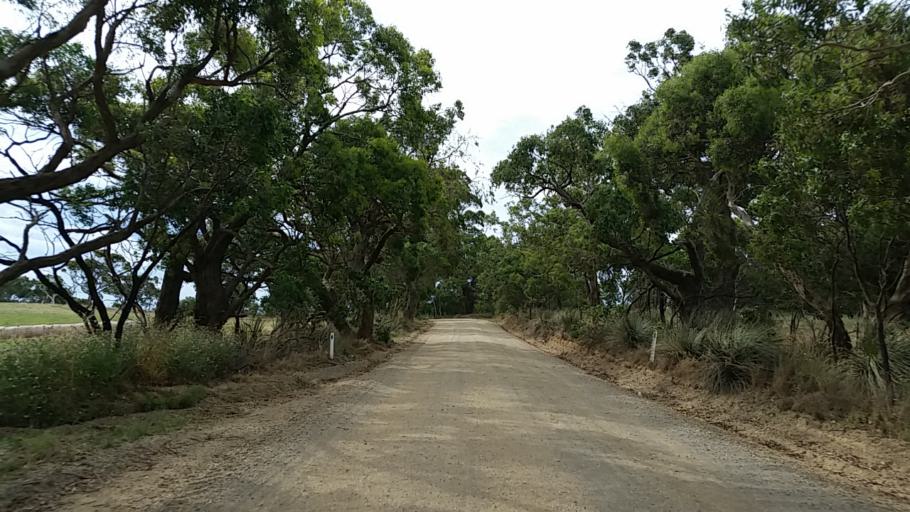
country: AU
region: South Australia
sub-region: Yankalilla
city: Normanville
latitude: -35.4120
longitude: 138.4228
